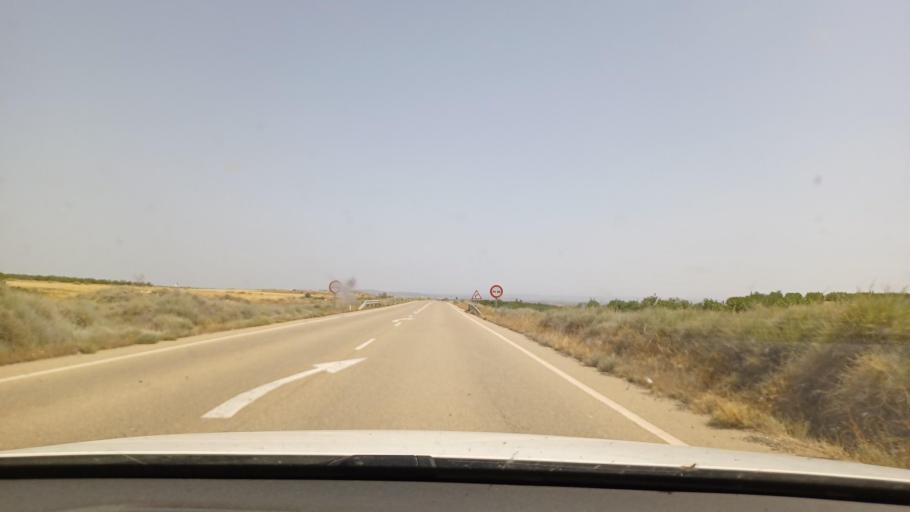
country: ES
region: Aragon
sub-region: Provincia de Zaragoza
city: Chiprana
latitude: 41.3236
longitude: -0.0805
